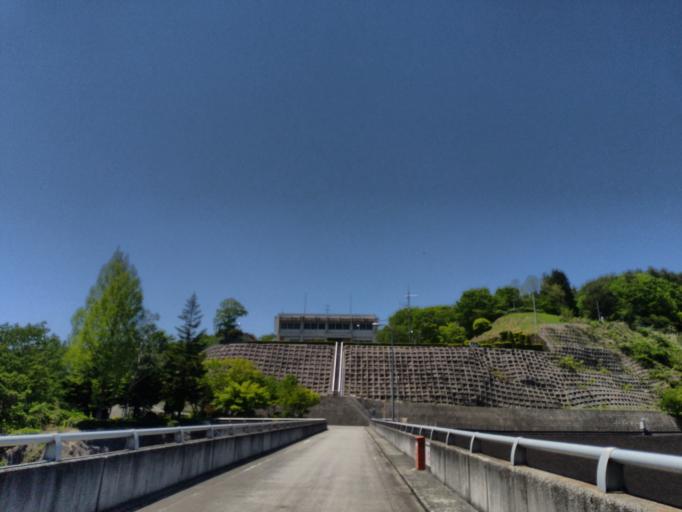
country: JP
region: Yamanashi
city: Nirasaki
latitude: 35.8746
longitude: 138.4342
